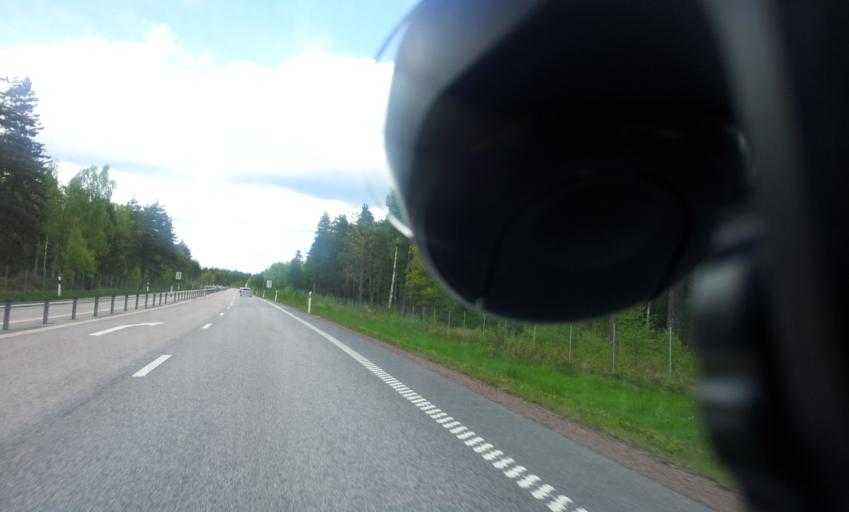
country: SE
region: Kalmar
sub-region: Oskarshamns Kommun
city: Paskallavik
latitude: 57.1068
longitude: 16.4990
